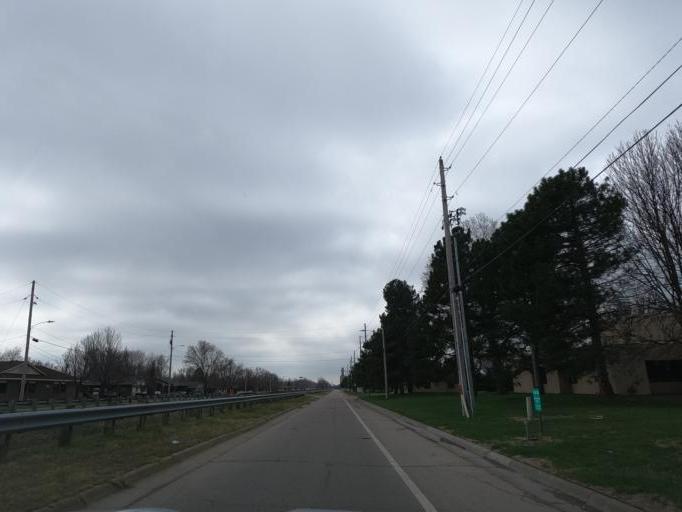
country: US
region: Kansas
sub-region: Reno County
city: Hutchinson
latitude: 38.0855
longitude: -97.9131
